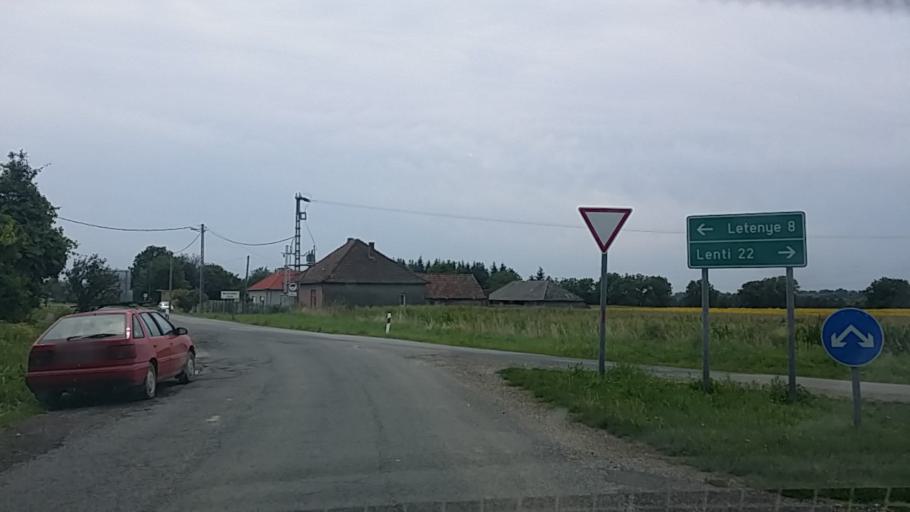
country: HR
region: Medimurska
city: Domasinec
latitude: 46.4814
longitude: 16.6533
